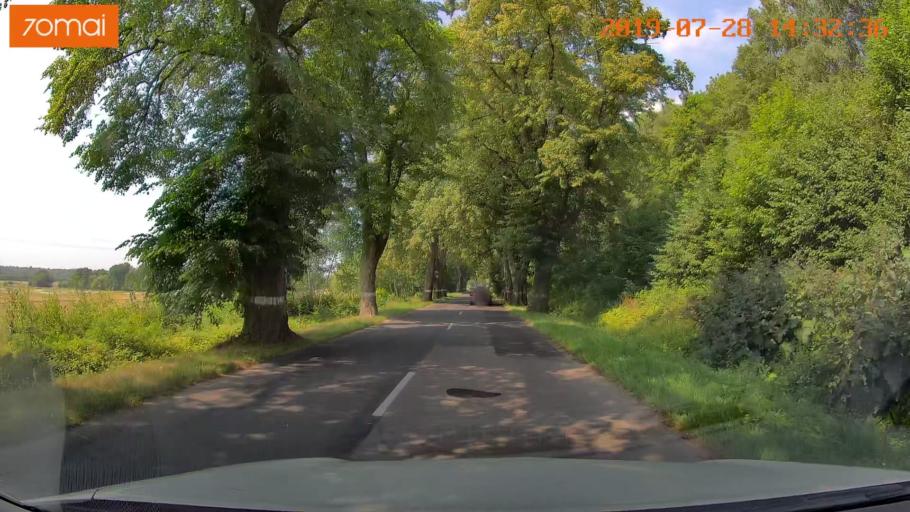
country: RU
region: Kaliningrad
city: Primorsk
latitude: 54.8138
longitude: 20.0399
